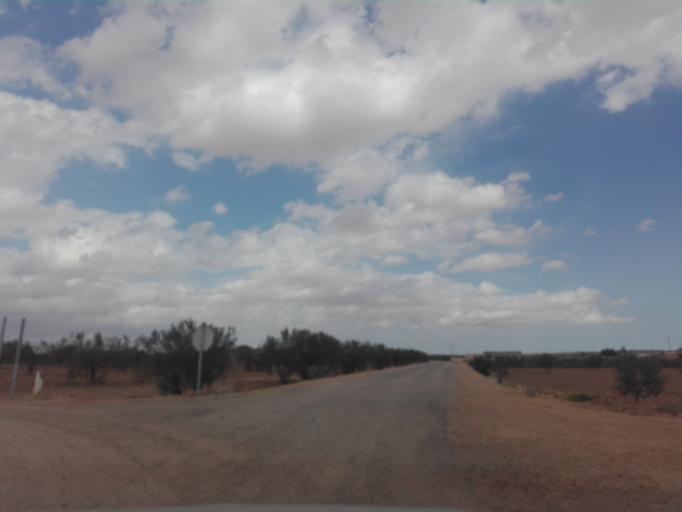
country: TN
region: Safaqis
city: Sfax
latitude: 34.6871
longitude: 10.4435
